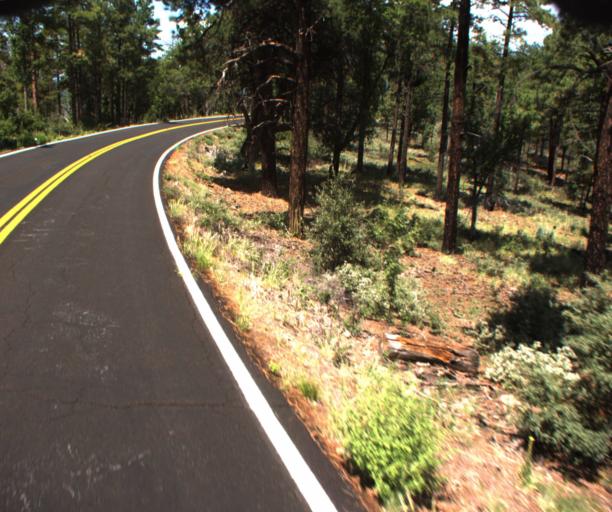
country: US
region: Arizona
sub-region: Greenlee County
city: Morenci
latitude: 33.4723
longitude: -109.3730
